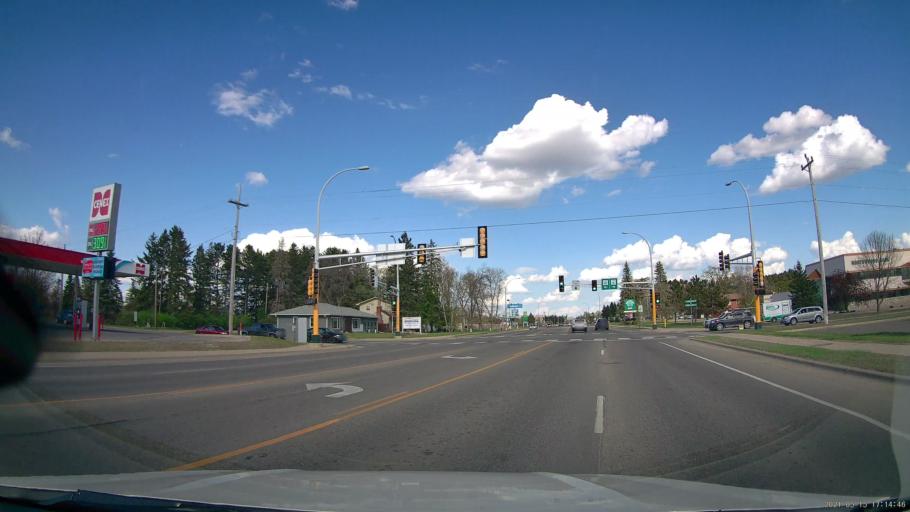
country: US
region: Minnesota
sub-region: Hubbard County
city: Park Rapids
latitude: 46.9217
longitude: -95.0376
